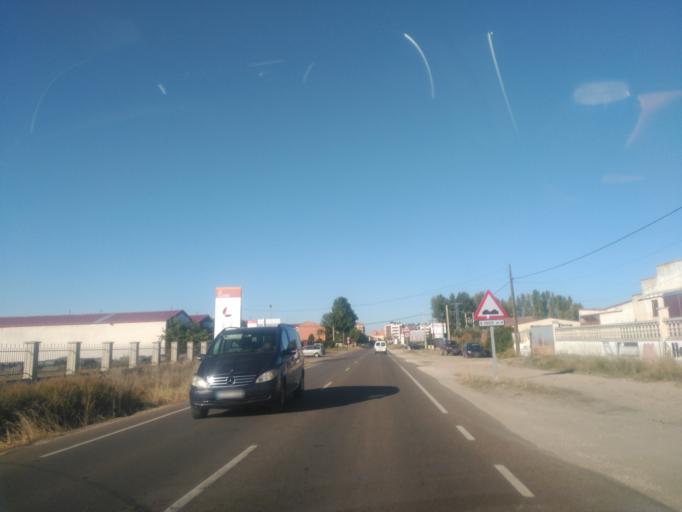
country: ES
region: Castille and Leon
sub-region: Provincia de Burgos
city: Aranda de Duero
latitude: 41.6742
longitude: -3.6697
